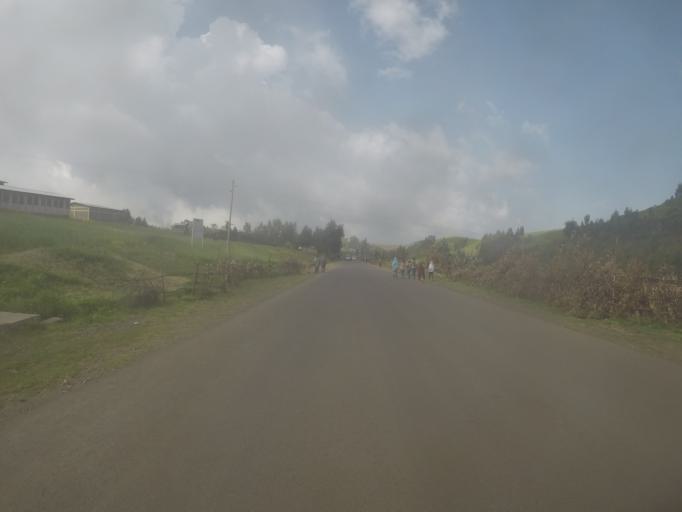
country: ET
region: Amhara
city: Gondar
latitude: 12.7701
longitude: 37.6296
